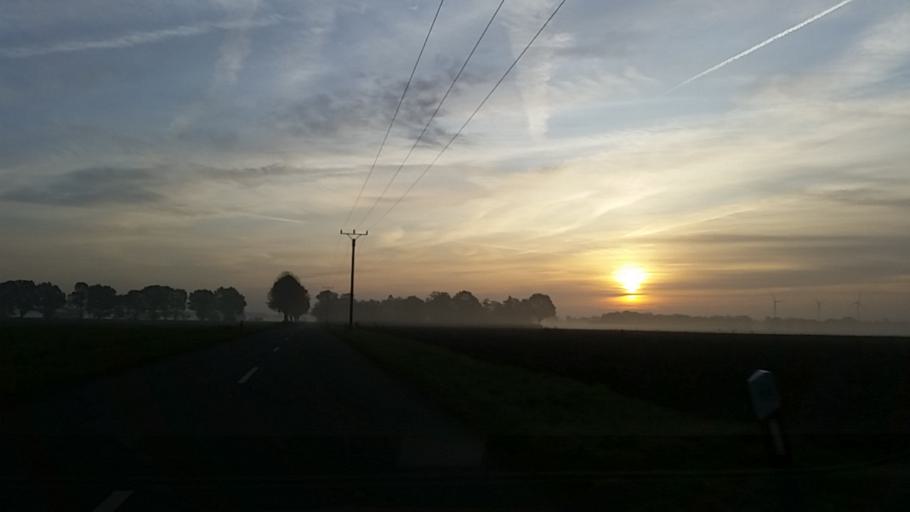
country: DE
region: Lower Saxony
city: Luder
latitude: 52.8039
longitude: 10.6820
